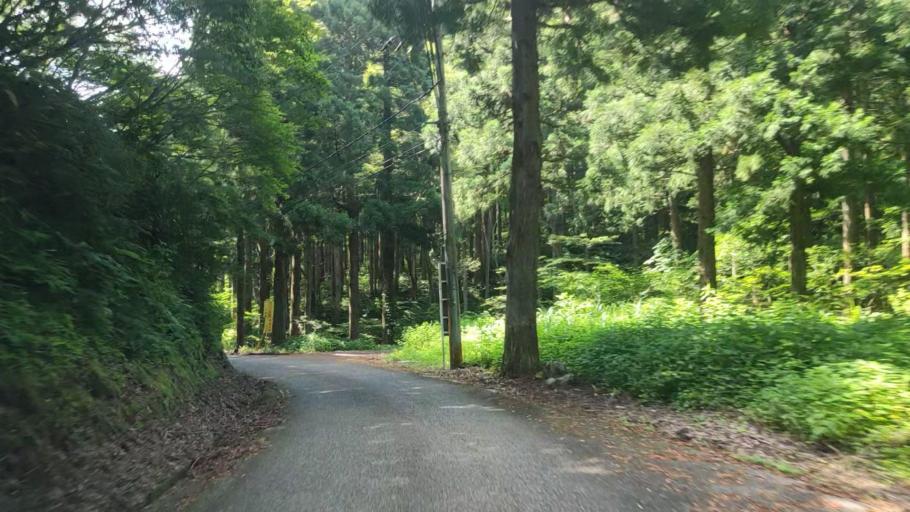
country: JP
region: Ishikawa
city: Komatsu
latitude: 36.2557
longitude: 136.5380
